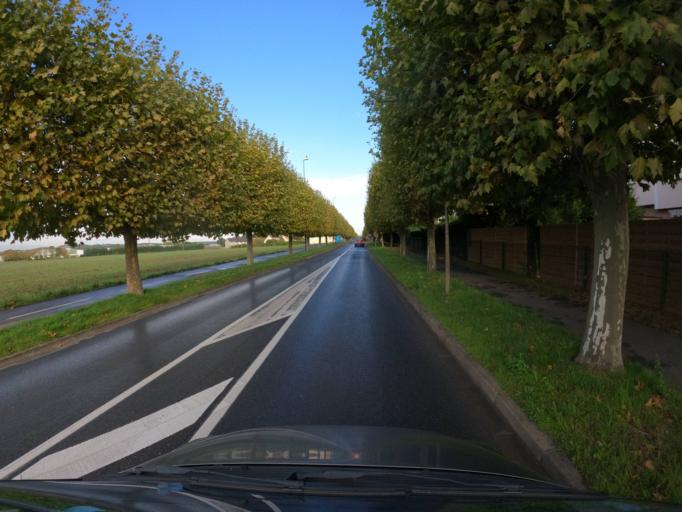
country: FR
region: Ile-de-France
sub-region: Departement de Seine-et-Marne
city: Brou-sur-Chantereine
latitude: 48.8899
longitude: 2.6195
